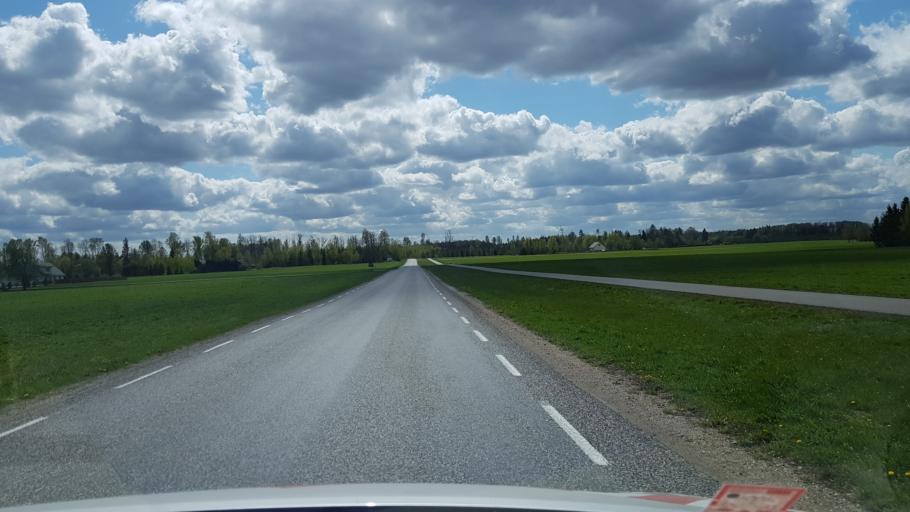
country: EE
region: Jogevamaa
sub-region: Poltsamaa linn
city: Poltsamaa
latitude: 58.7013
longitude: 25.9413
